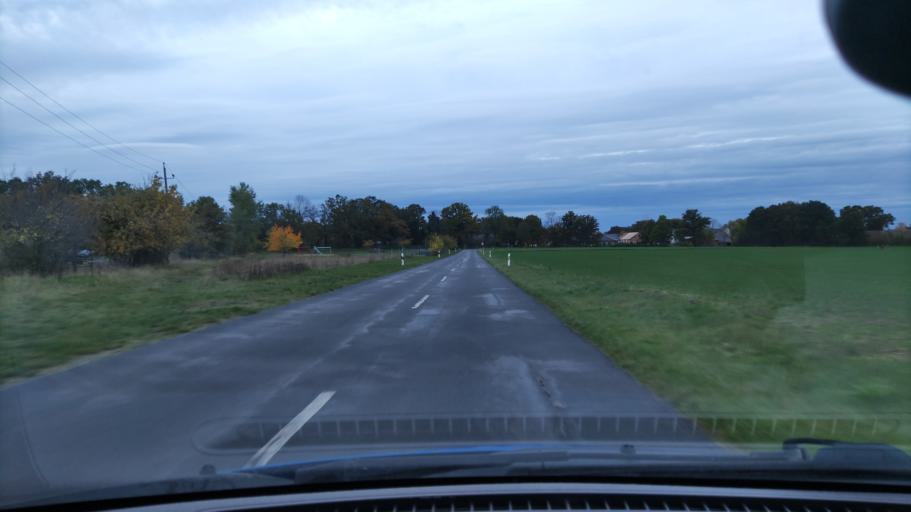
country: DE
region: Saxony-Anhalt
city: Luftkurort Arendsee
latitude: 52.8939
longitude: 11.4488
